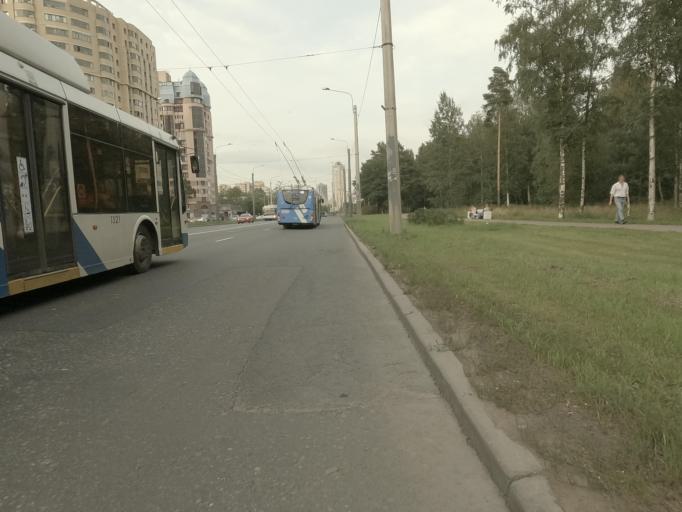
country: RU
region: St.-Petersburg
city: Dachnoye
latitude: 59.8366
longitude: 30.2282
